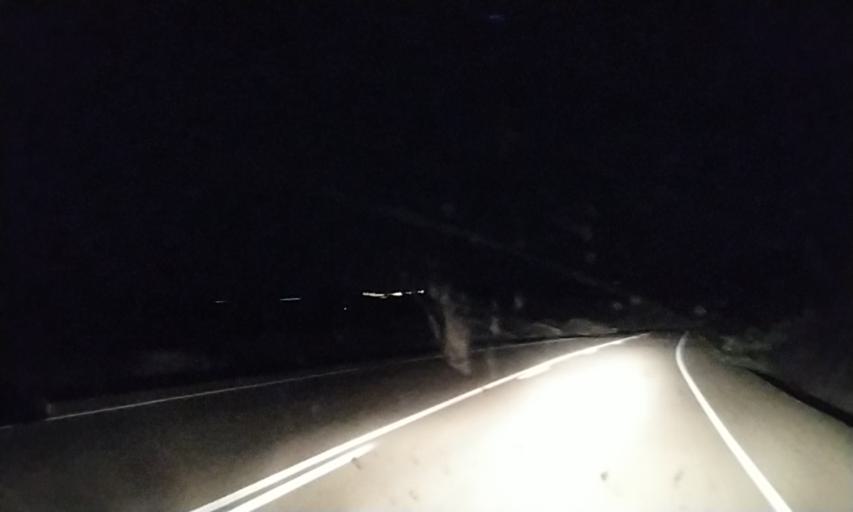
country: ES
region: Castille and Leon
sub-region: Provincia de Salamanca
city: Pastores
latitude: 40.5000
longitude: -6.5772
